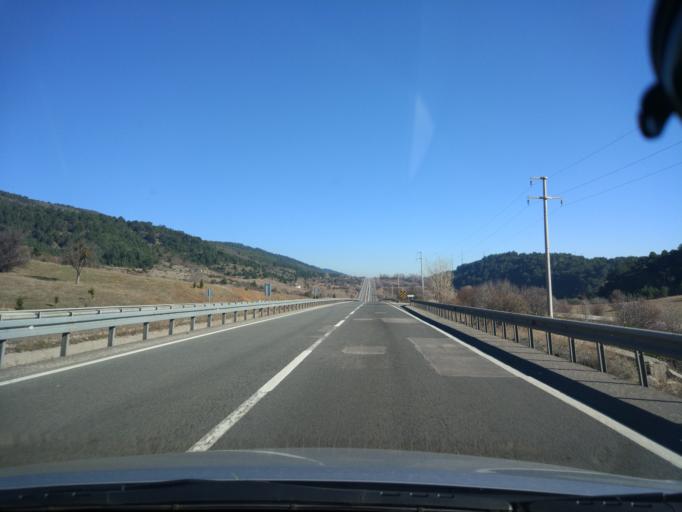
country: TR
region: Bolu
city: Gerede
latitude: 40.8114
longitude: 32.2646
